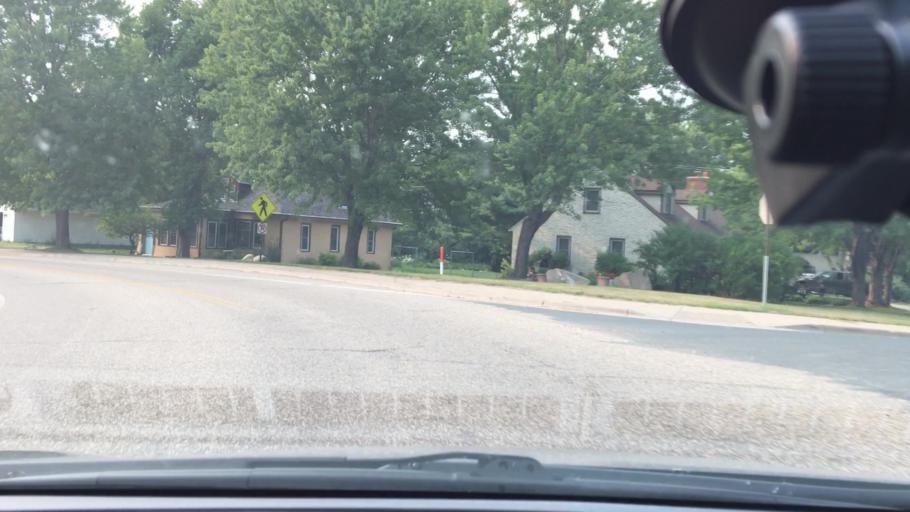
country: US
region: Minnesota
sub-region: Hennepin County
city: Dayton
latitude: 45.2440
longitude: -93.5152
